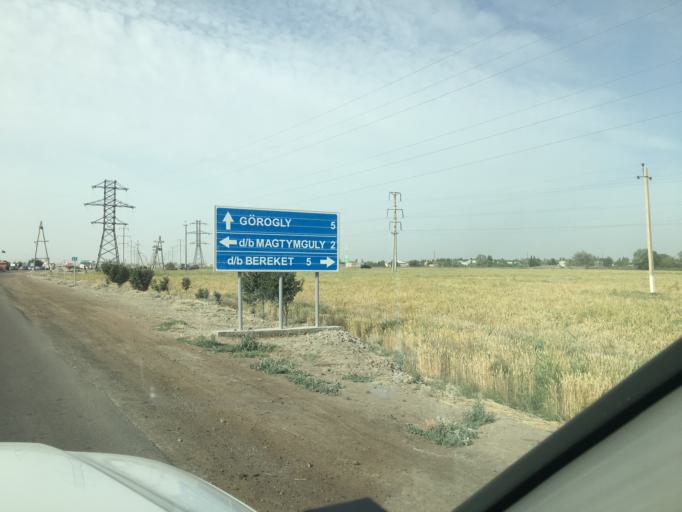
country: TM
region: Dasoguz
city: Tagta
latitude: 41.6952
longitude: 59.9315
